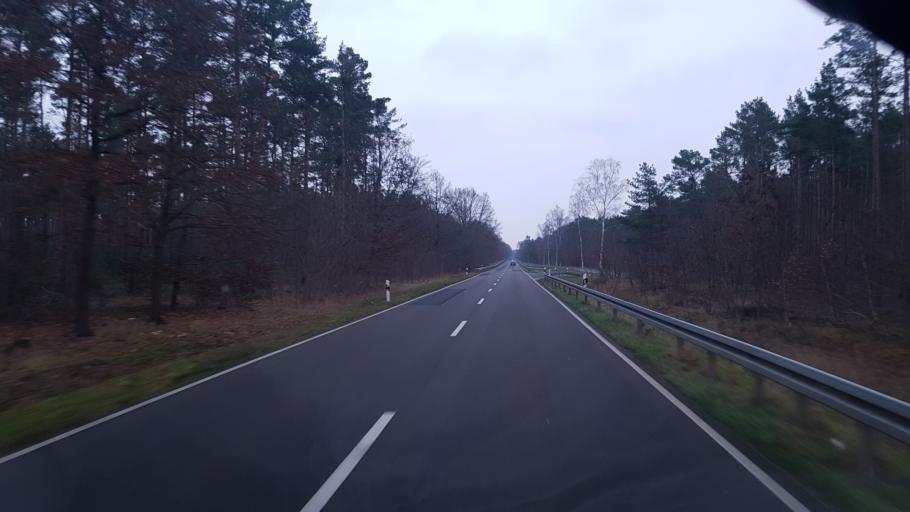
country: DE
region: Brandenburg
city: Tauer
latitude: 51.9068
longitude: 14.4782
